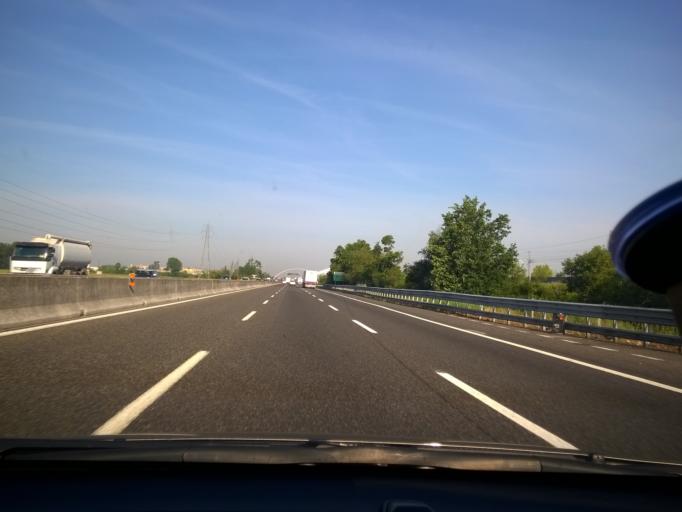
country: IT
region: Emilia-Romagna
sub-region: Provincia di Reggio Emilia
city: Massenzatico
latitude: 44.7220
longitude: 10.6635
